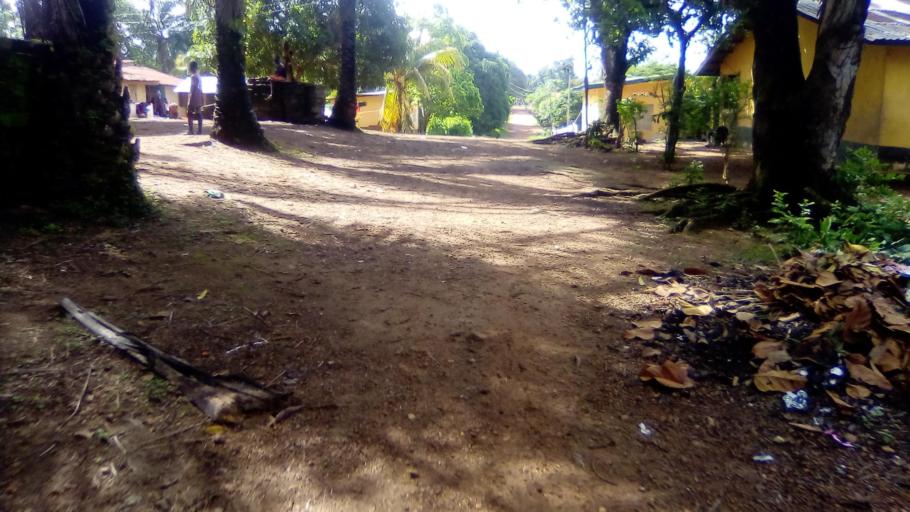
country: SL
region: Southern Province
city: Bo
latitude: 7.9778
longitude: -11.7297
